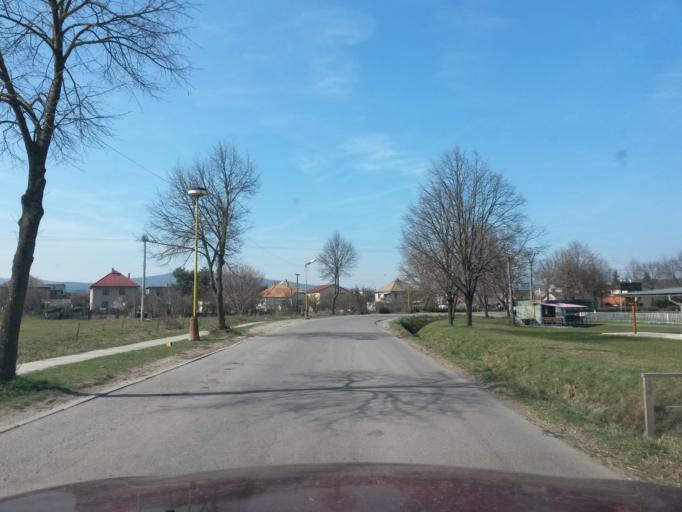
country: SK
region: Banskobystricky
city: Lucenec
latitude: 48.3674
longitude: 19.6261
